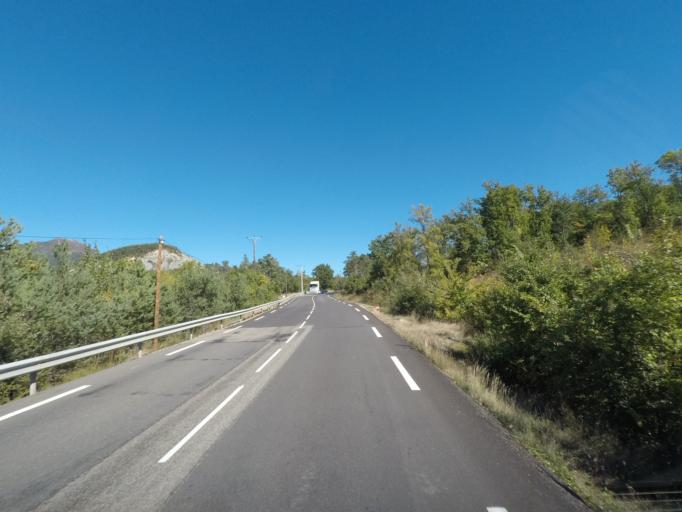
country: FR
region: Rhone-Alpes
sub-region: Departement de la Drome
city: Buis-les-Baronnies
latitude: 44.3781
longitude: 5.4461
